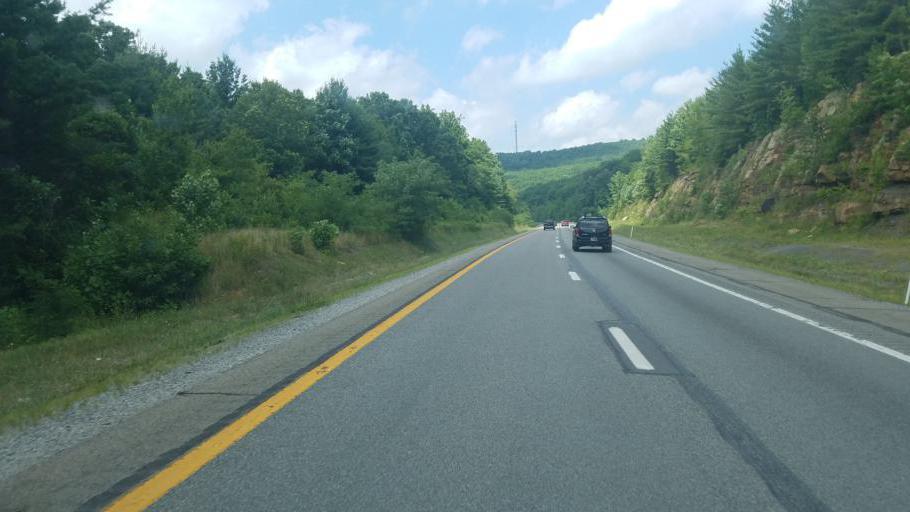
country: US
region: West Virginia
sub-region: Raleigh County
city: Shady Spring
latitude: 37.6895
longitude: -81.1288
